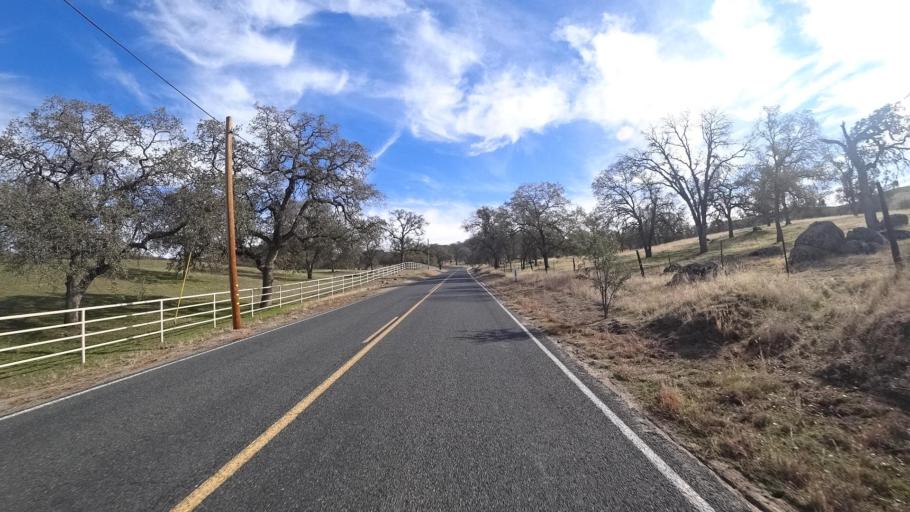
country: US
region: California
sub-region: Kern County
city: Oildale
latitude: 35.6273
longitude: -118.8274
